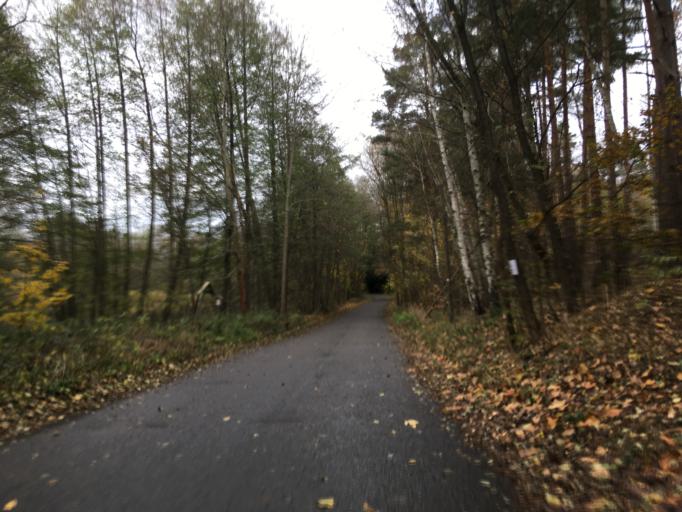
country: DE
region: Brandenburg
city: Mixdorf
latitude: 52.0984
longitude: 14.4329
